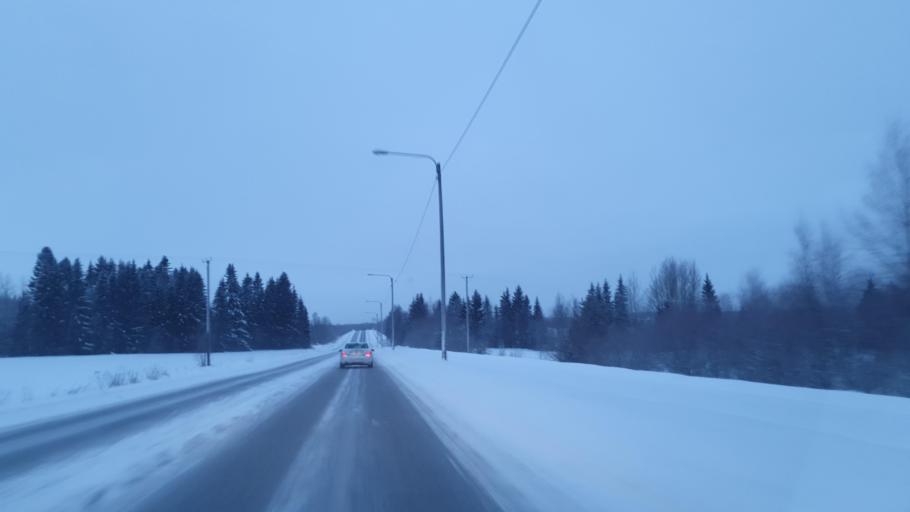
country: FI
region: Northern Ostrobothnia
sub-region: Oulu
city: Muhos
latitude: 64.7996
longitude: 26.0459
